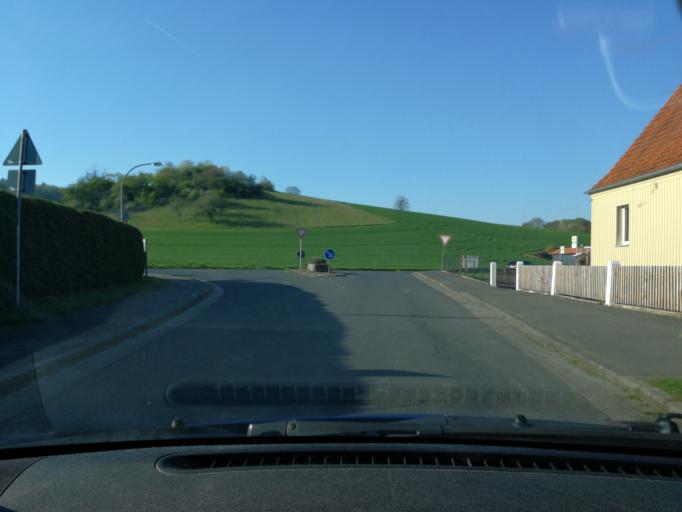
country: DE
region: Lower Saxony
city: Adelebsen
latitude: 51.5878
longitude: 9.8097
